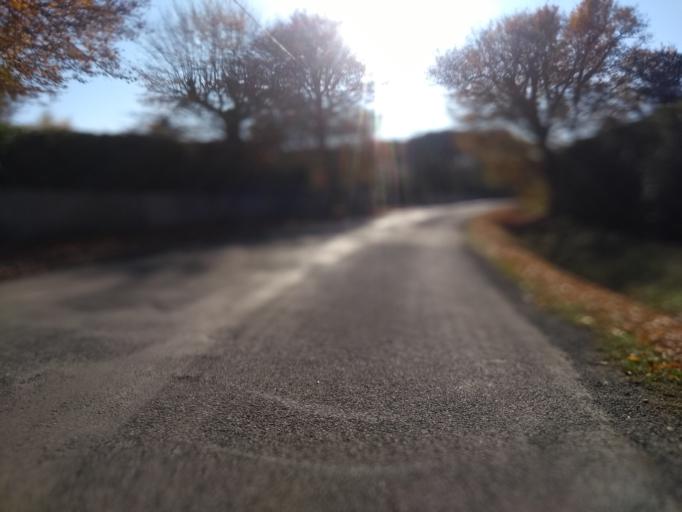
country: FR
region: Aquitaine
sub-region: Departement de la Gironde
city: Leognan
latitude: 44.7370
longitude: -0.5998
